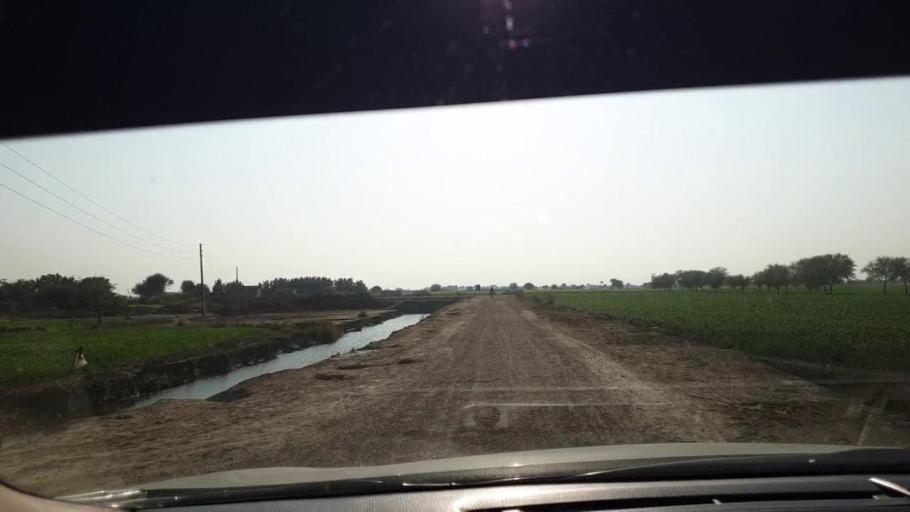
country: PK
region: Sindh
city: Berani
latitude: 25.8115
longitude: 68.7810
